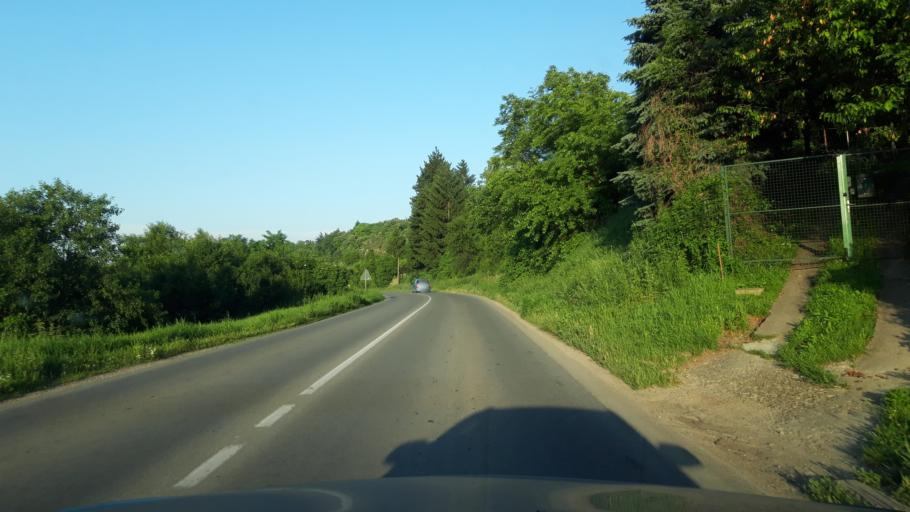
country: RS
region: Autonomna Pokrajina Vojvodina
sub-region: Juznobacki Okrug
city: Beocin
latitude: 45.2088
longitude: 19.7558
